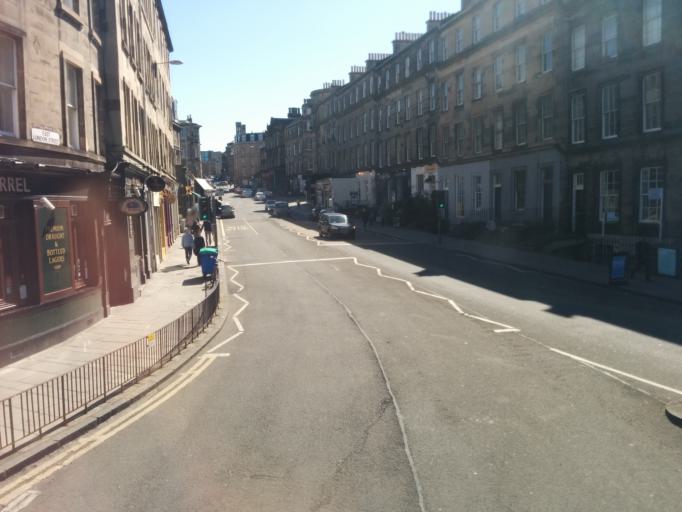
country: GB
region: Scotland
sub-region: Edinburgh
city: Edinburgh
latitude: 55.9592
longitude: -3.1906
